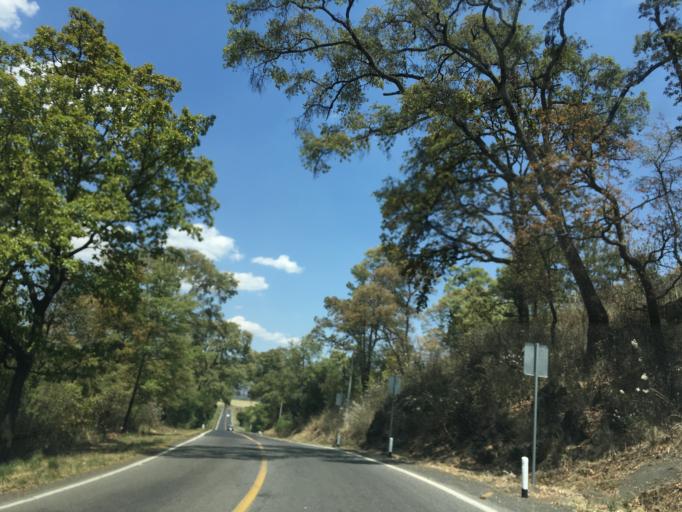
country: MX
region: Mexico
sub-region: Chalco
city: Zopoco
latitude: 19.7850
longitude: -102.0226
